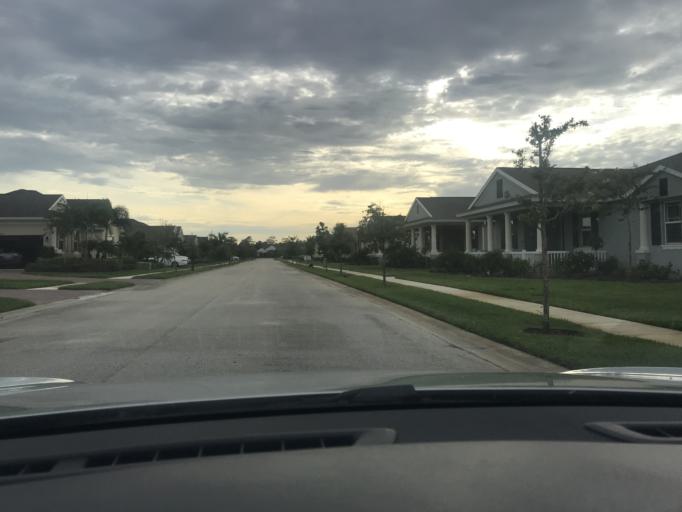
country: US
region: Florida
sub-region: Indian River County
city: West Vero Corridor
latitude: 27.6269
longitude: -80.4745
